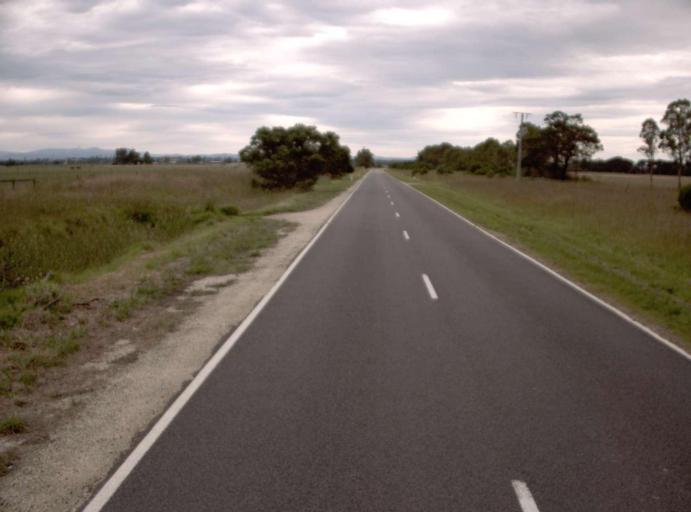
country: AU
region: Victoria
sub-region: Wellington
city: Sale
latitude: -38.0559
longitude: 147.1485
